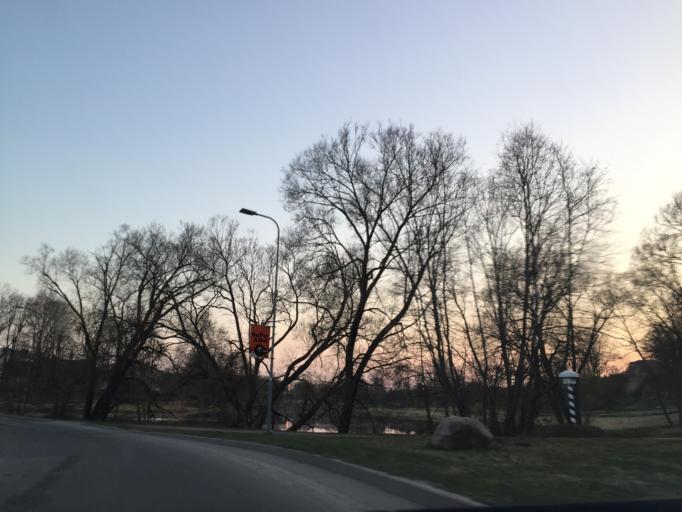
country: LV
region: Valkas Rajons
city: Valka
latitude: 57.7801
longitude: 26.0271
